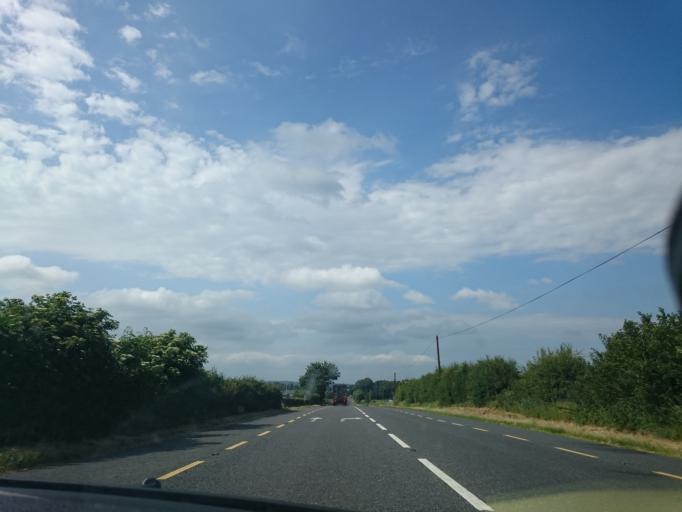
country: IE
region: Leinster
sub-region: Kilkenny
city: Kilkenny
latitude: 52.6153
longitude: -7.2467
